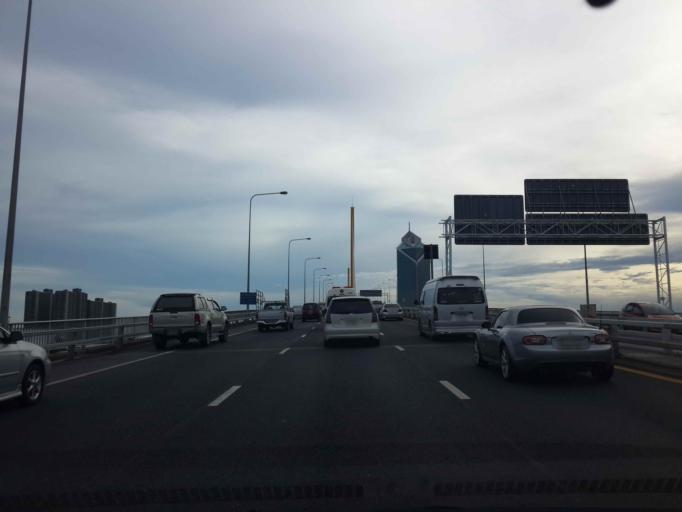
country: TH
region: Bangkok
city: Rat Burana
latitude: 13.6875
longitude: 100.5218
